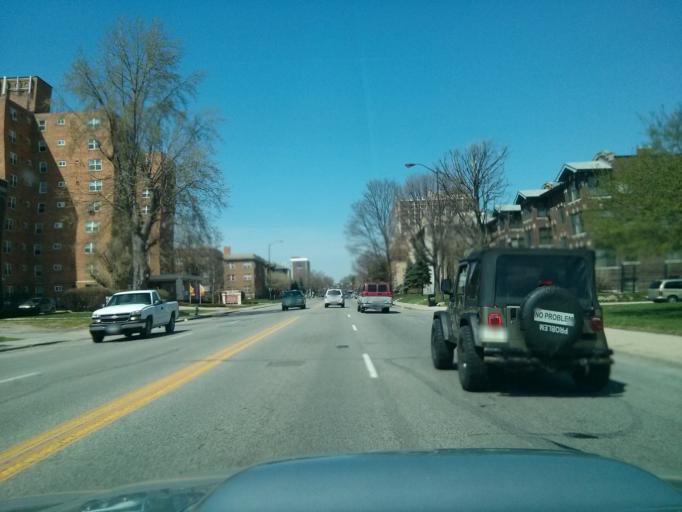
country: US
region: Indiana
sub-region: Marion County
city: Broad Ripple
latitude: 39.8218
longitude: -86.1568
